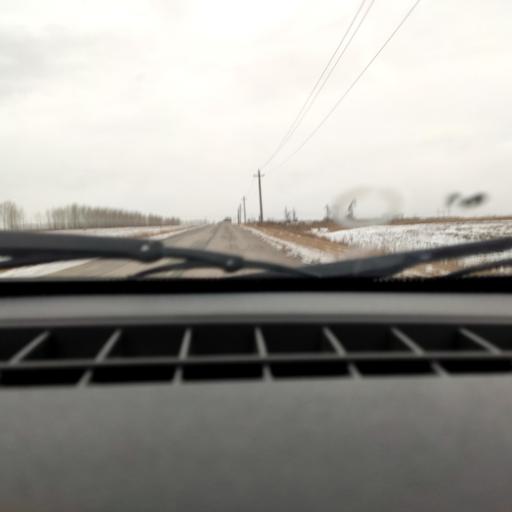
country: RU
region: Bashkortostan
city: Tolbazy
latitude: 54.2485
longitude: 55.8968
